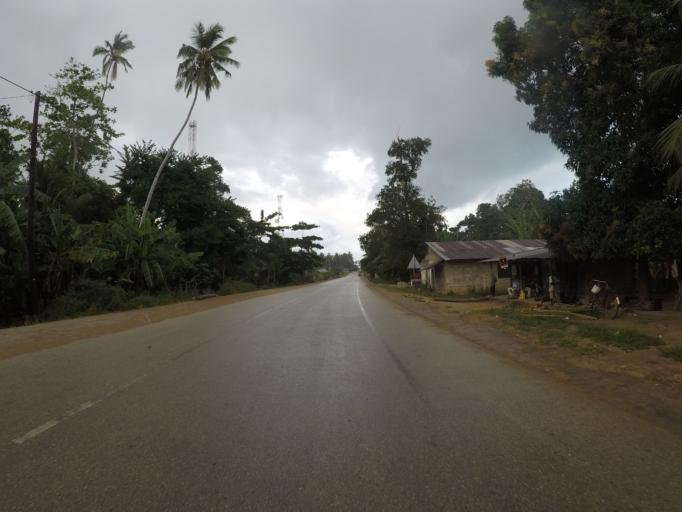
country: TZ
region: Zanzibar North
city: Mkokotoni
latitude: -5.9679
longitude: 39.1967
